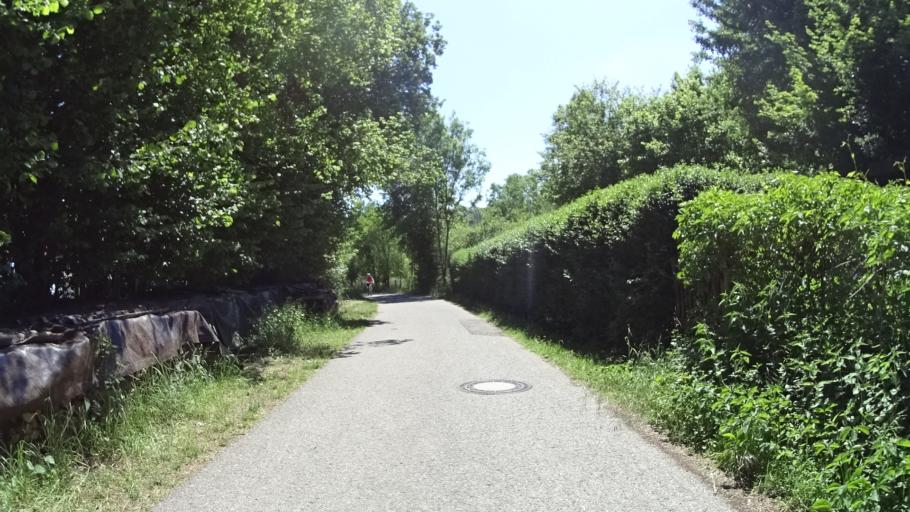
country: DE
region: Bavaria
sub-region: Regierungsbezirk Mittelfranken
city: Rothenburg ob der Tauber
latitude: 49.3884
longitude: 10.1661
